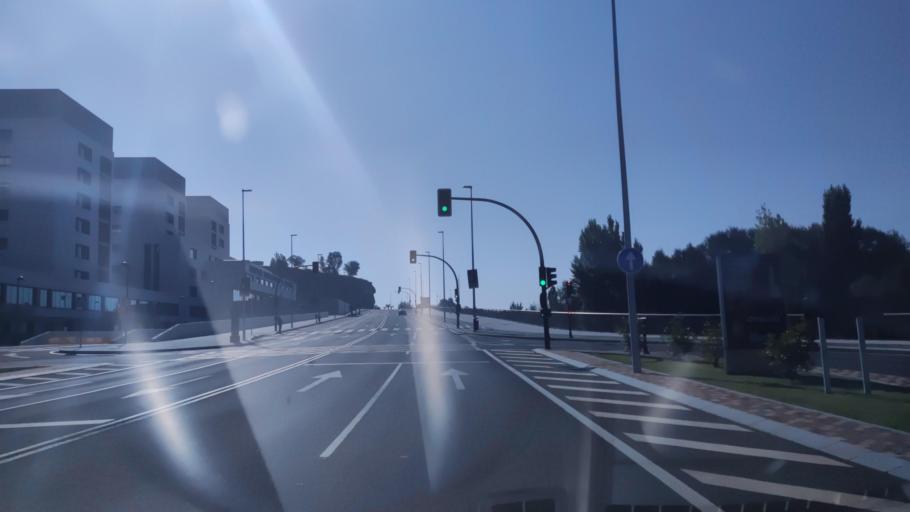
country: ES
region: Castille and Leon
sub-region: Provincia de Salamanca
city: Salamanca
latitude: 40.9632
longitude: -5.6777
